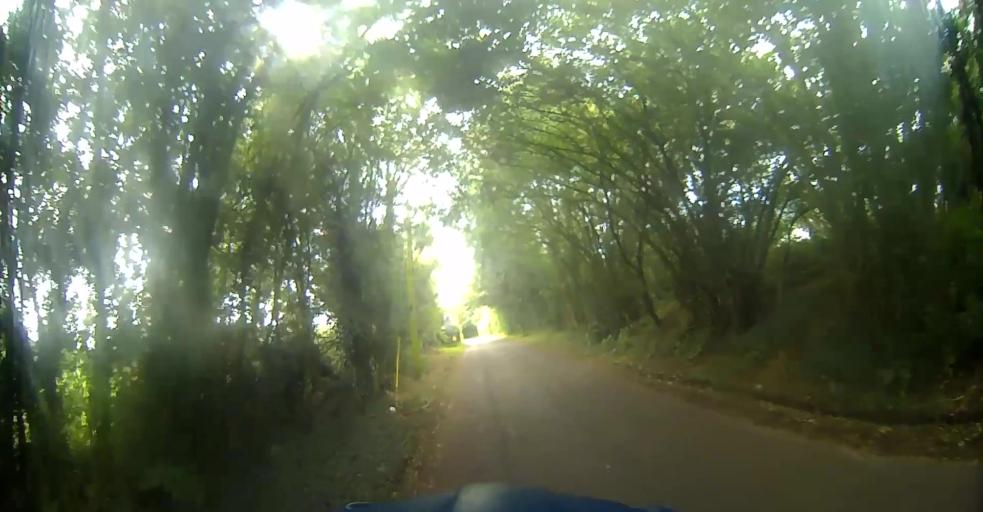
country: GB
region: England
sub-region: Hampshire
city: Alton
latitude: 51.1794
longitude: -1.0295
